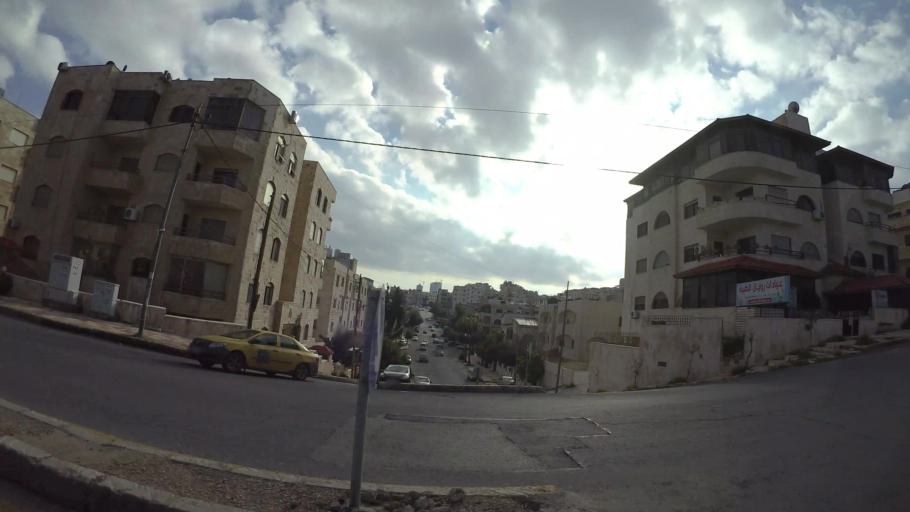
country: JO
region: Amman
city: Al Jubayhah
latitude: 31.9775
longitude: 35.8864
